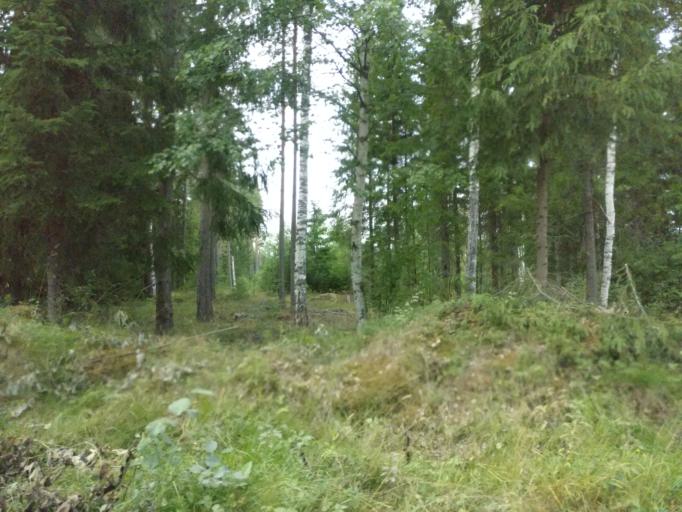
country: SE
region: Vaermland
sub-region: Hagfors Kommun
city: Hagfors
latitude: 60.0116
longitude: 13.6941
